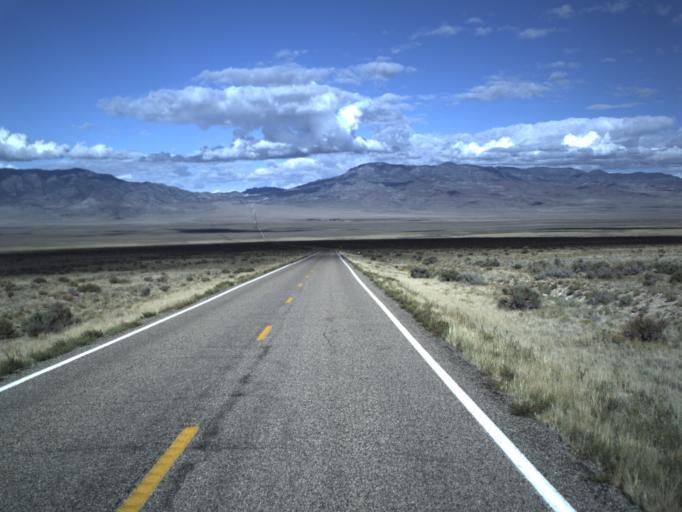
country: US
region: Utah
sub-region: Beaver County
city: Milford
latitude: 38.4406
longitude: -113.3174
